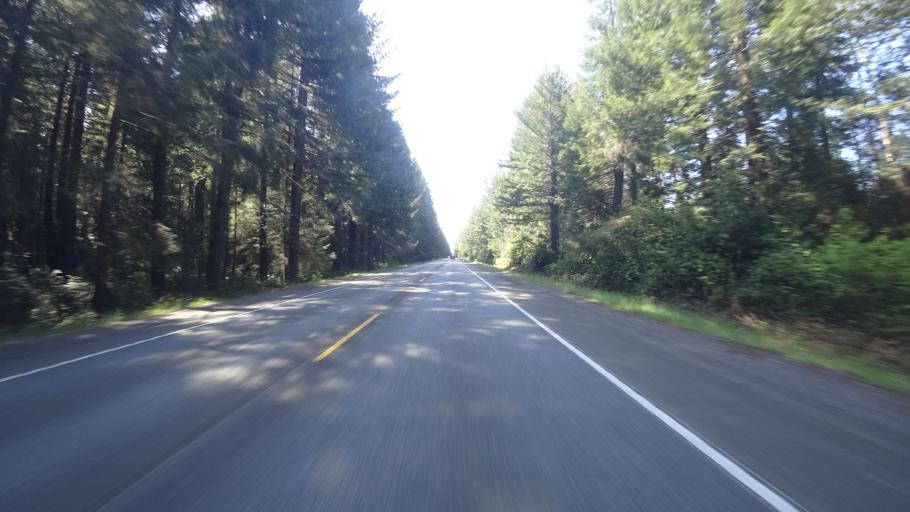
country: US
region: California
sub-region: Del Norte County
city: Bertsch-Oceanview
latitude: 41.8436
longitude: -124.1434
